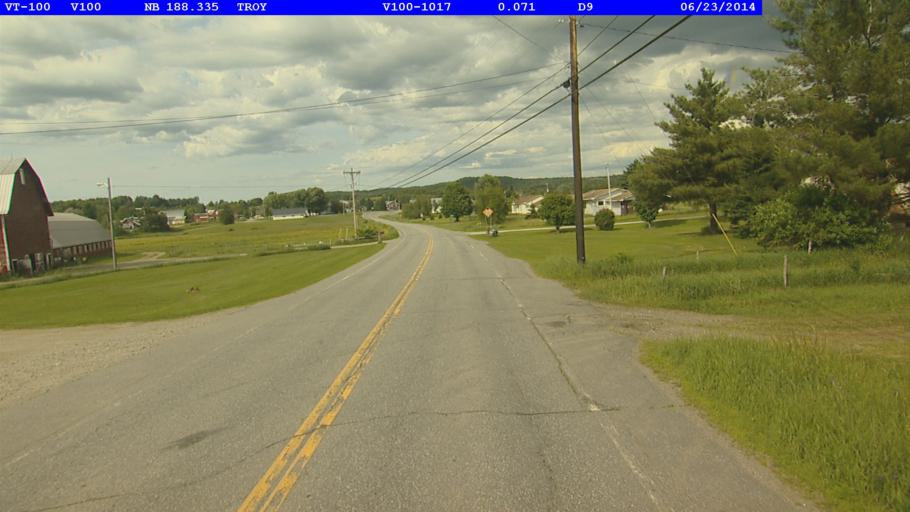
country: US
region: Vermont
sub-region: Orleans County
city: Newport
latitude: 44.9001
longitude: -72.4092
